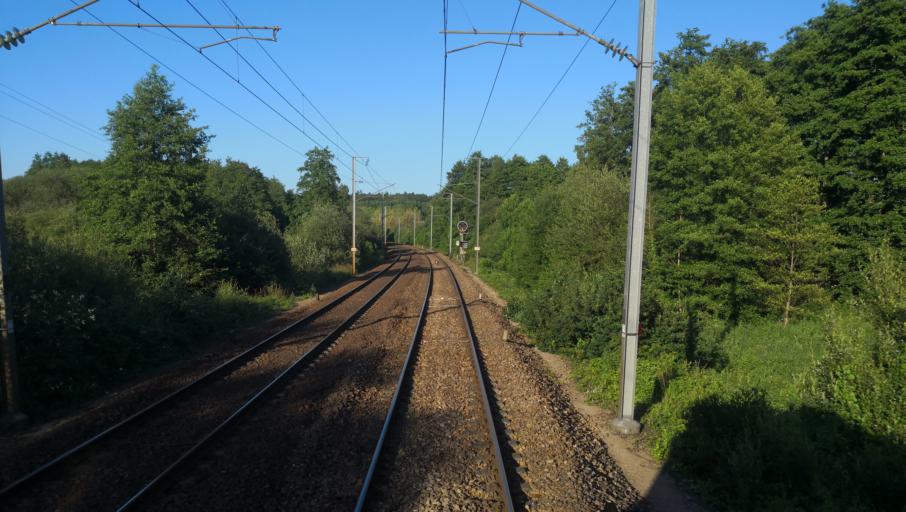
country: FR
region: Haute-Normandie
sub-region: Departement de l'Eure
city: Serquigny
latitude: 49.0915
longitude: 0.6837
